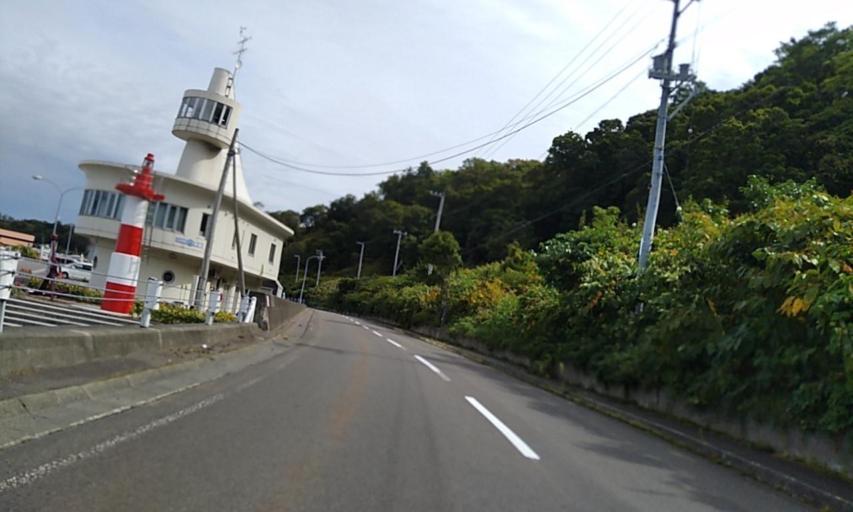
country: JP
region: Hokkaido
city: Rumoi
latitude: 43.8512
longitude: 141.5337
